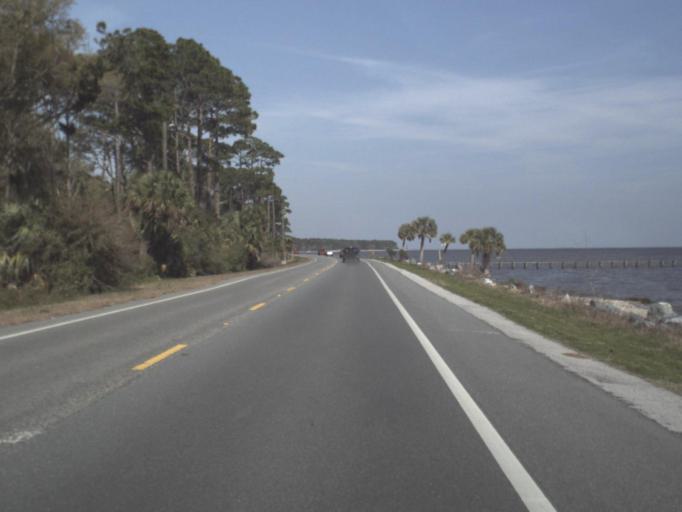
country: US
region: Florida
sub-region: Franklin County
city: Eastpoint
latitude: 29.7506
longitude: -84.8485
